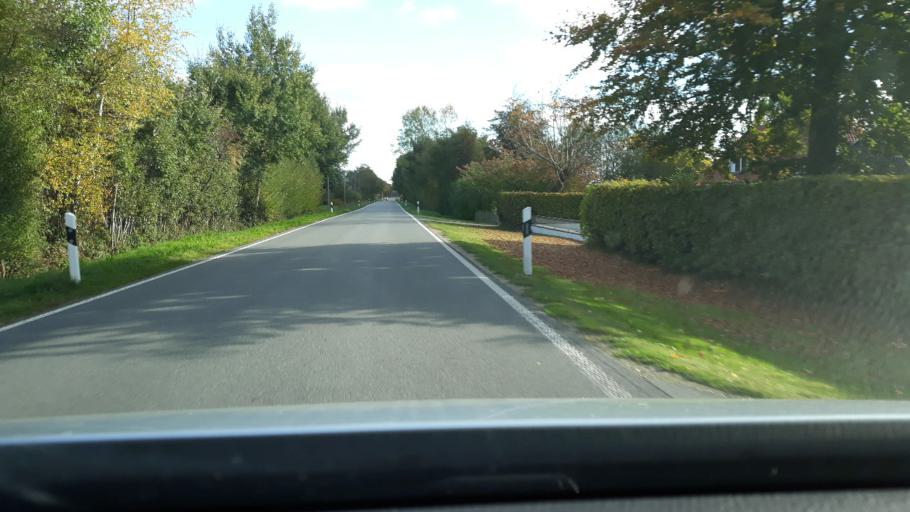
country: DE
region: Schleswig-Holstein
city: Idstedt
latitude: 54.5958
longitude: 9.4862
